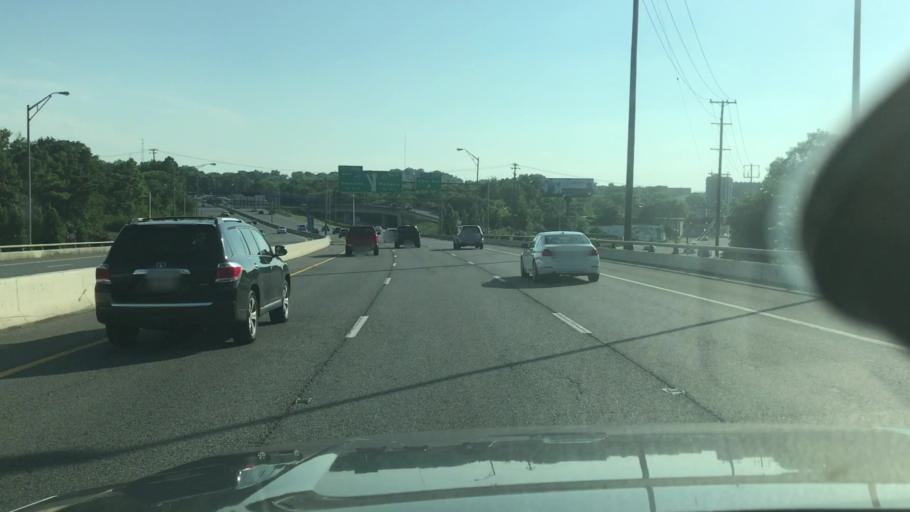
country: US
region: Tennessee
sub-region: Davidson County
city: Nashville
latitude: 36.1695
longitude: -86.8143
